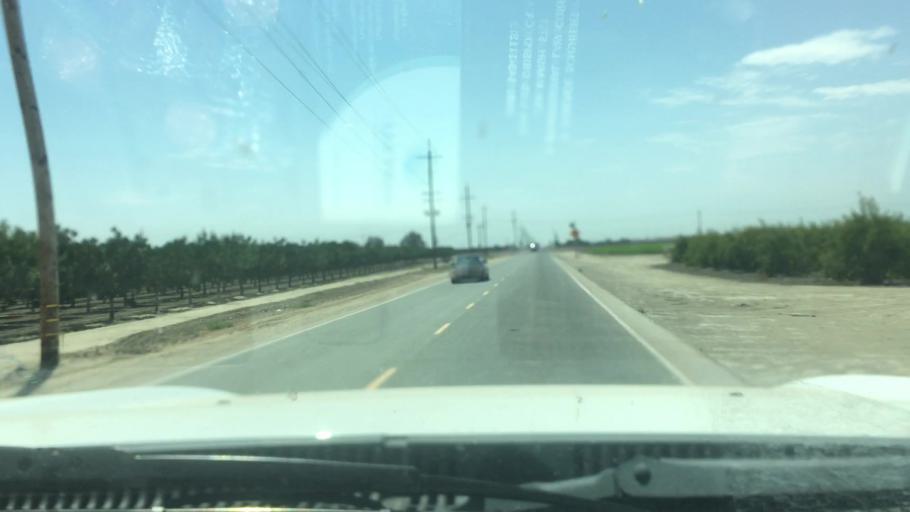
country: US
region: California
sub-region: Kings County
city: Corcoran
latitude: 36.0508
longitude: -119.5181
